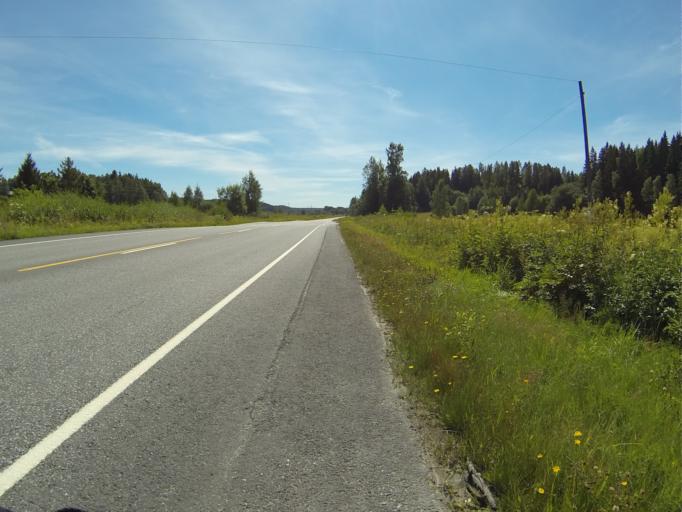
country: FI
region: Varsinais-Suomi
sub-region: Salo
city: Salo
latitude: 60.3035
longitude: 23.1063
